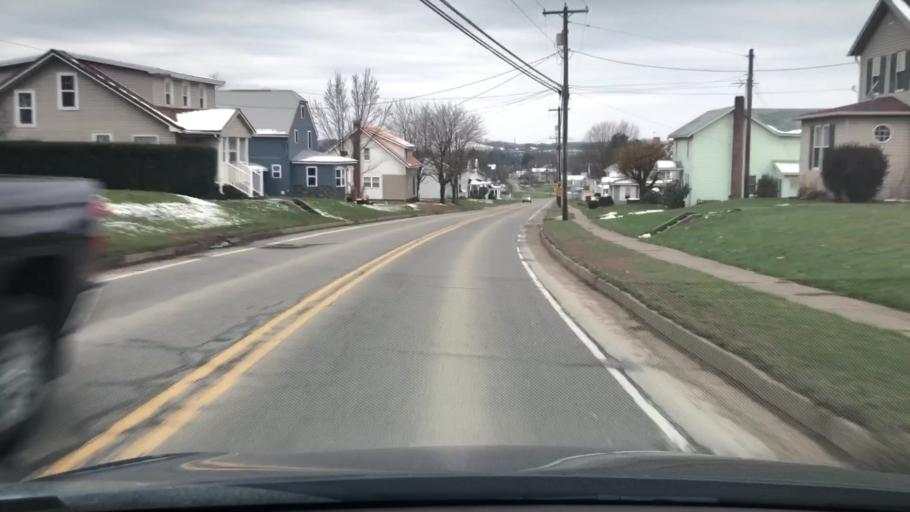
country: US
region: Pennsylvania
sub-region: Armstrong County
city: Kittanning
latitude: 40.9706
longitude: -79.3538
